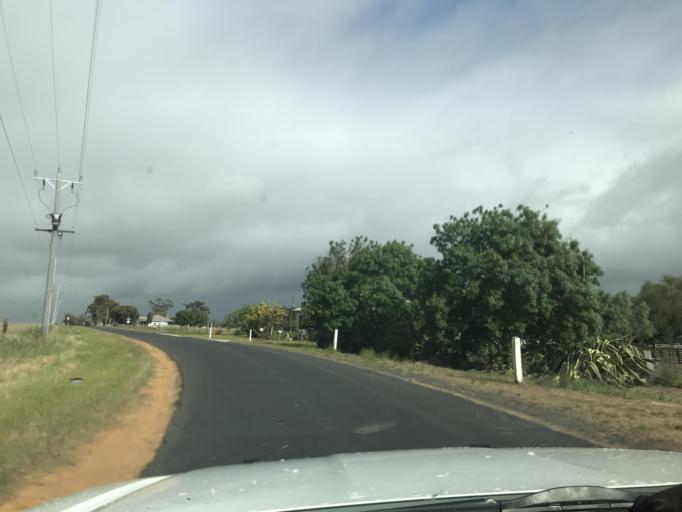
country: AU
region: South Australia
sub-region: Tatiara
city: Bordertown
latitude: -36.3668
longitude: 141.2404
